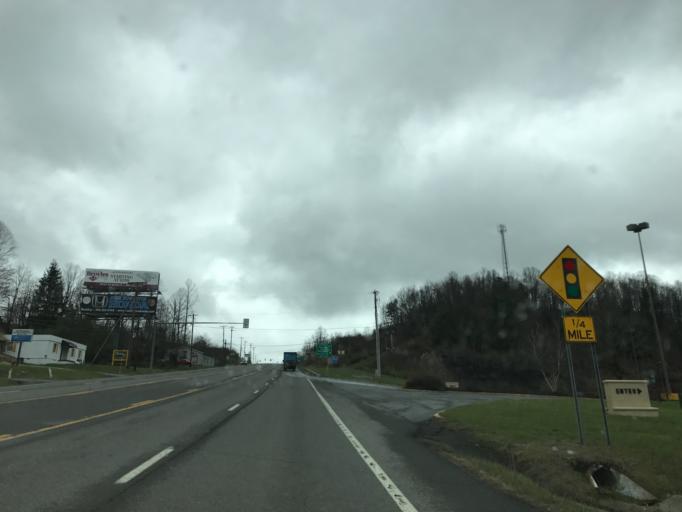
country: US
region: West Virginia
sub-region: Raleigh County
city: Prosperity
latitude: 37.8465
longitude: -81.1953
